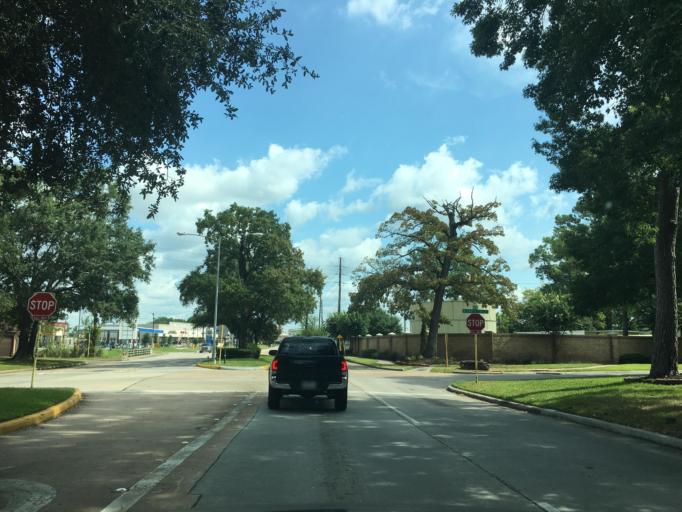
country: US
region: Texas
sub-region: Harris County
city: Spring
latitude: 30.0491
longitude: -95.4388
